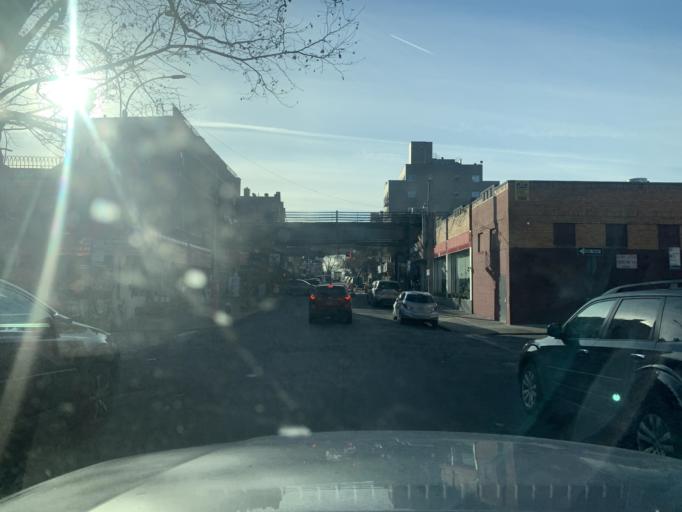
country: US
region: New York
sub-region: Queens County
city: Long Island City
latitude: 40.7476
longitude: -73.8897
